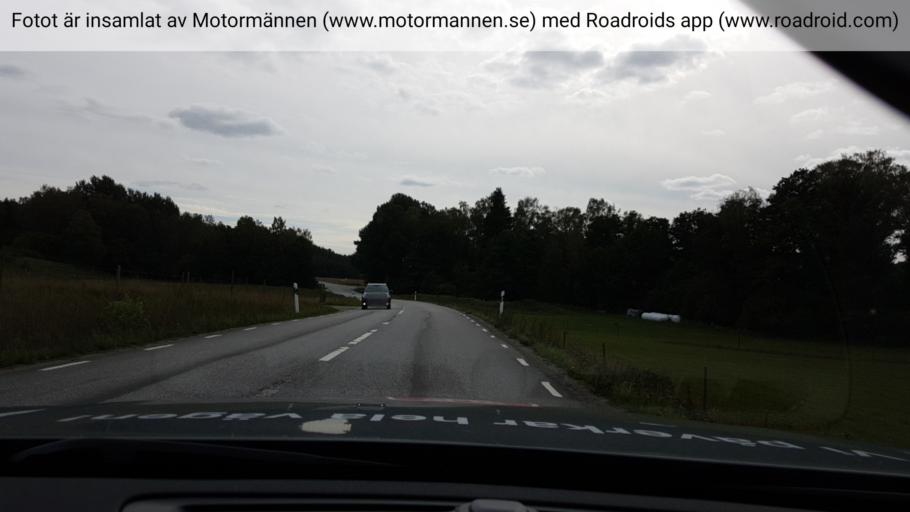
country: SE
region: Stockholm
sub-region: Botkyrka Kommun
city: Varsta
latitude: 59.1076
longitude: 17.8018
